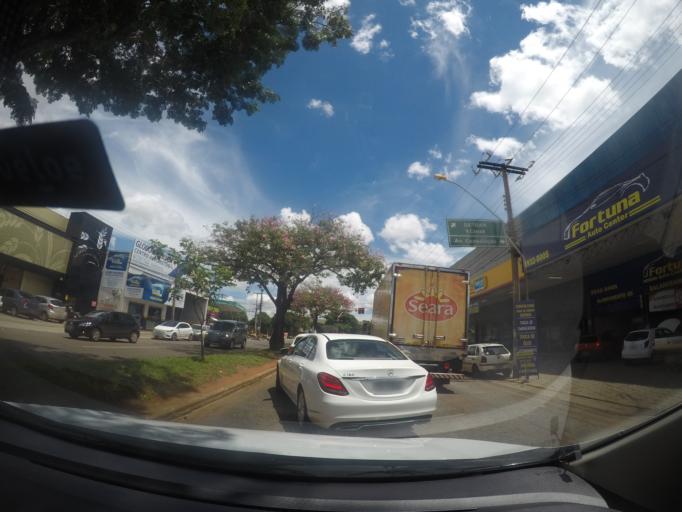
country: BR
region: Goias
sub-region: Goiania
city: Goiania
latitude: -16.6801
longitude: -49.3079
